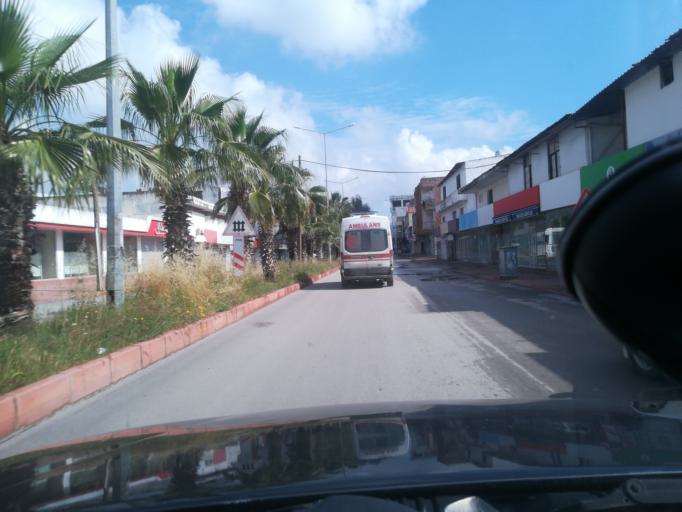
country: TR
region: Adana
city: Yuregir
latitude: 36.9828
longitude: 35.4305
